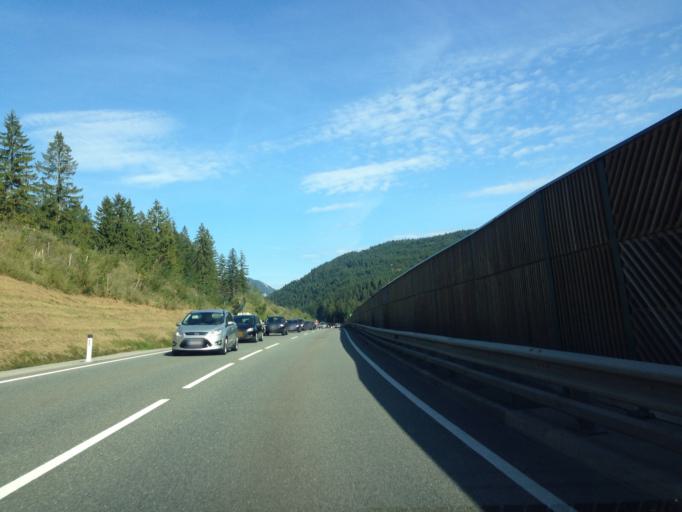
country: AT
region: Tyrol
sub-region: Politischer Bezirk Reutte
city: Heiterwang
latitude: 47.4429
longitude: 10.7415
